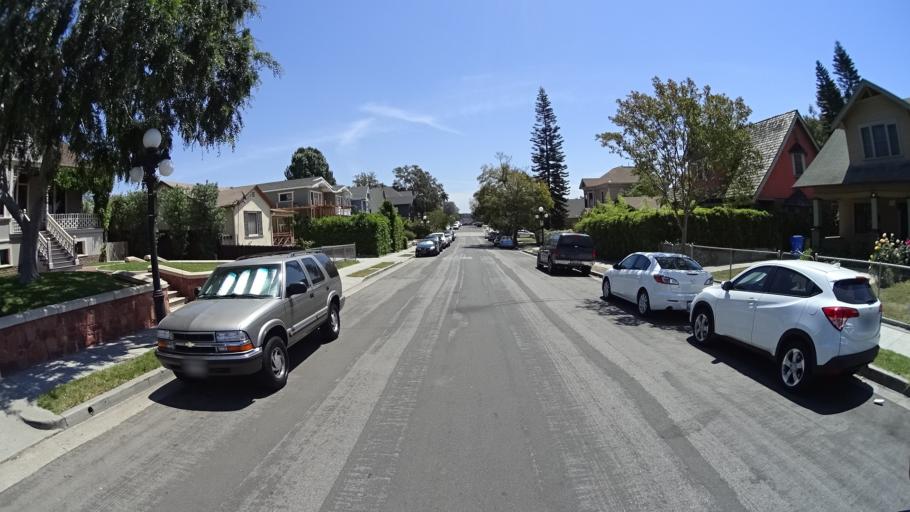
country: US
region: California
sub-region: Los Angeles County
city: Echo Park
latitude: 34.0701
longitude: -118.2562
